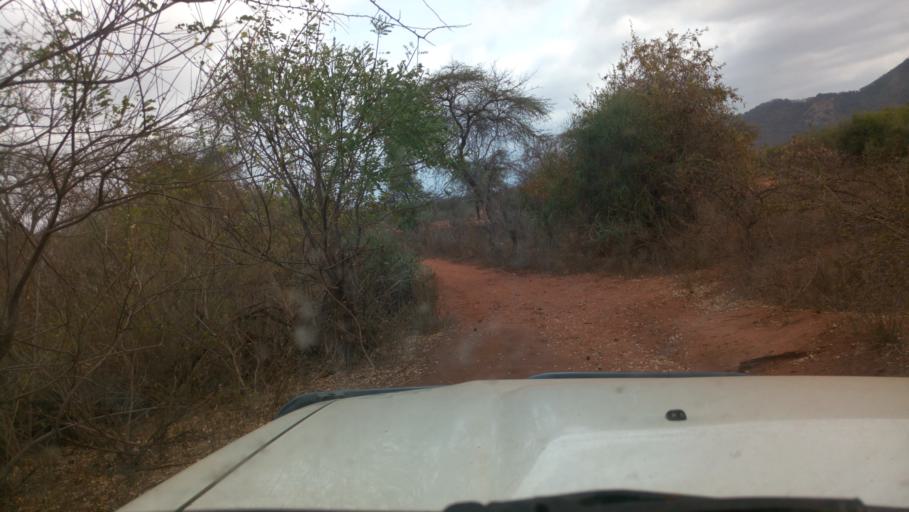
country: KE
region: Kitui
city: Kitui
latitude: -1.8289
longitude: 38.3220
